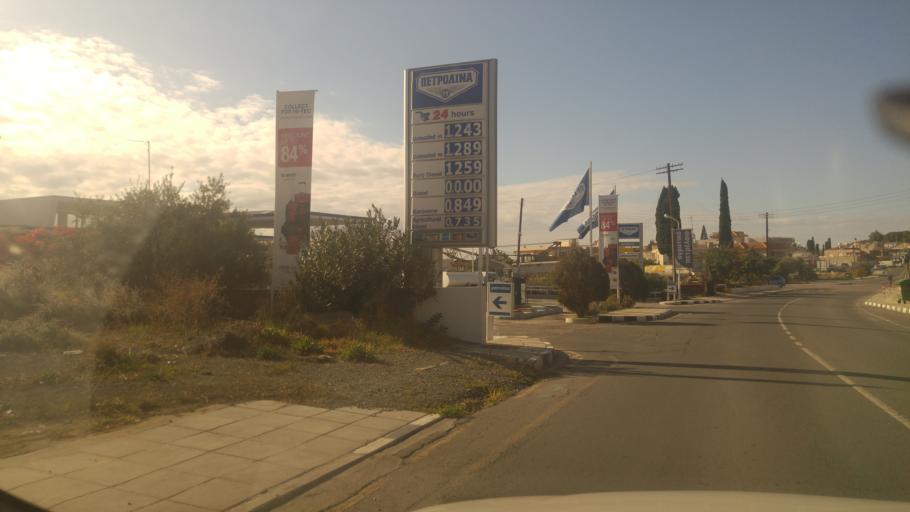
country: CY
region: Larnaka
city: Kolossi
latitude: 34.6721
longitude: 32.9374
